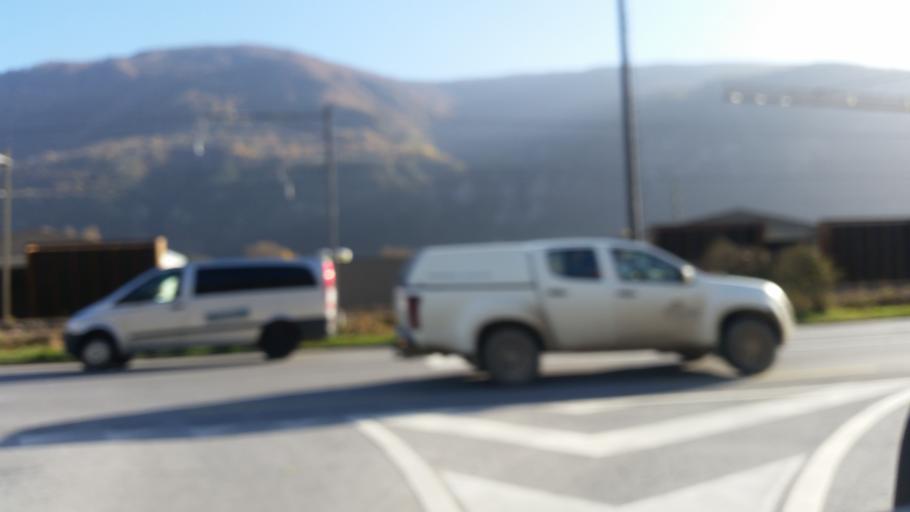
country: CH
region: Valais
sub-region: Sierre District
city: Grone
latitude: 46.2613
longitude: 7.4471
